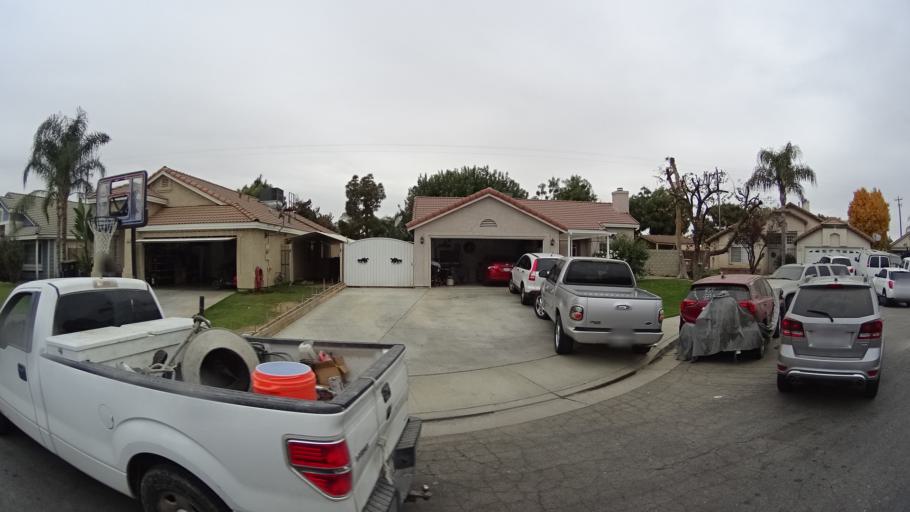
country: US
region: California
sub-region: Kern County
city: Greenfield
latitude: 35.2860
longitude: -119.0472
